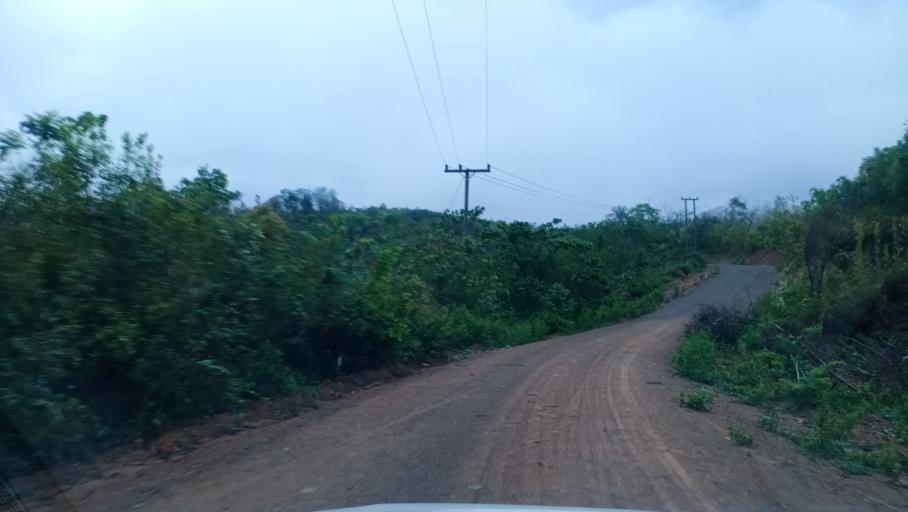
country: LA
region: Phongsali
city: Khoa
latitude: 21.3066
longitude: 102.7032
